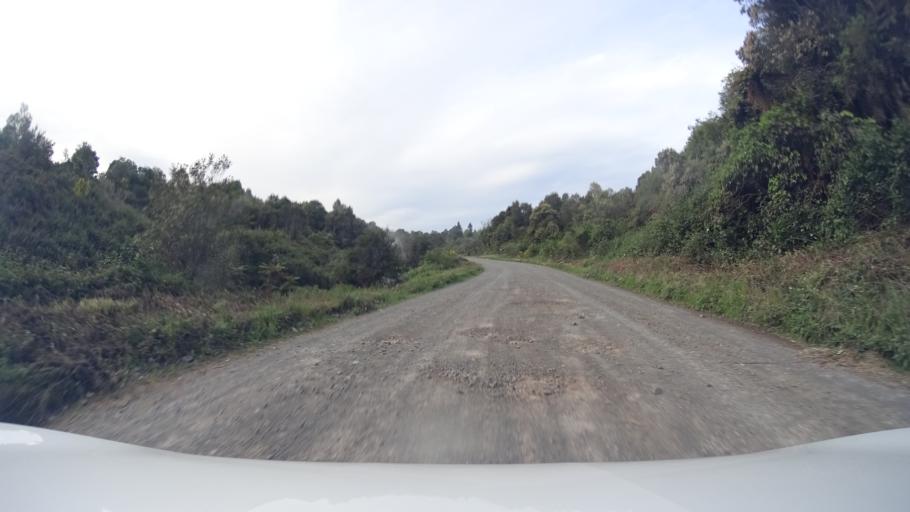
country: NZ
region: Bay of Plenty
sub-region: Rotorua District
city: Rotorua
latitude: -38.3252
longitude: 176.3738
